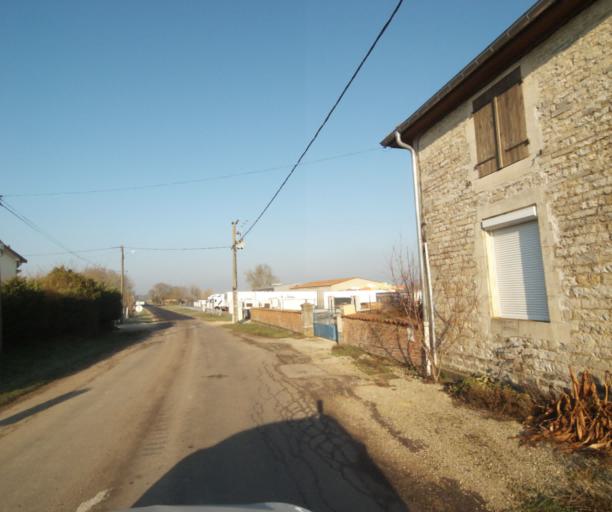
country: FR
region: Champagne-Ardenne
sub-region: Departement de la Haute-Marne
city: Montier-en-Der
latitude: 48.4819
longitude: 4.7496
